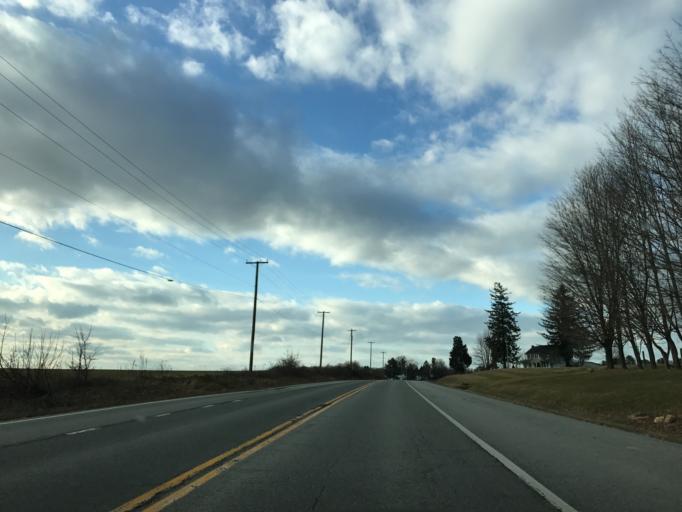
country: US
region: Maryland
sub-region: Cecil County
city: Rising Sun
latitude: 39.6796
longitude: -76.0334
